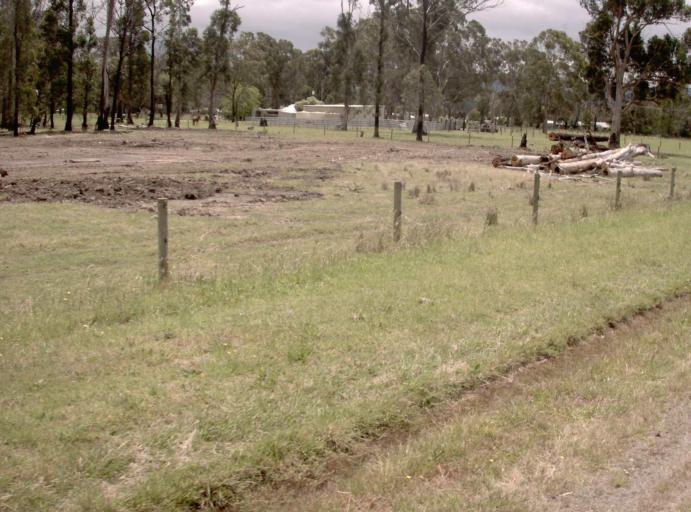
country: AU
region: Victoria
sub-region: Latrobe
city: Traralgon
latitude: -38.5317
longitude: 146.6585
